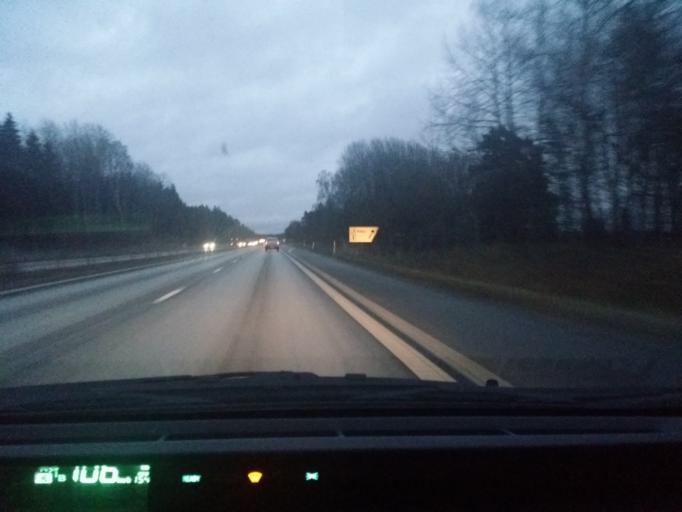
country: SE
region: Vaestmanland
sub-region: Vasteras
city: Skultuna
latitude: 59.5878
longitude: 16.3913
